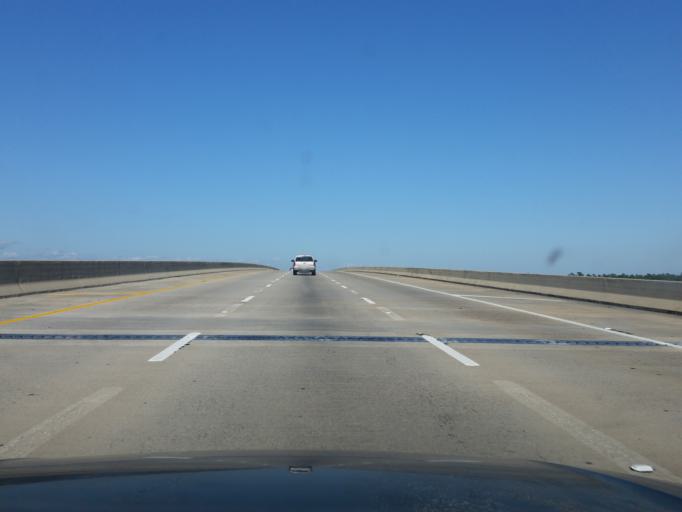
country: US
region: Mississippi
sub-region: Hancock County
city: Diamondhead
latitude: 30.3641
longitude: -89.4044
